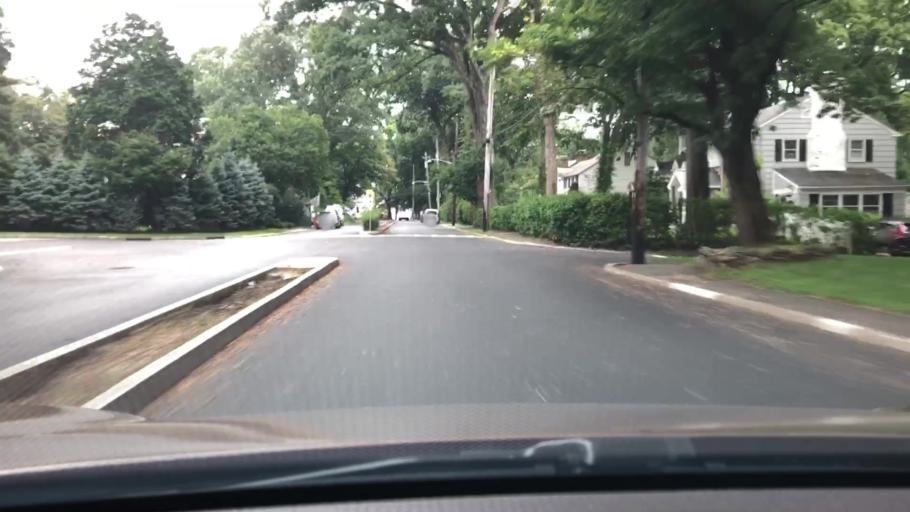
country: US
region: New York
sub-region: Westchester County
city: Tuckahoe
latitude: 40.9438
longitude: -73.8255
